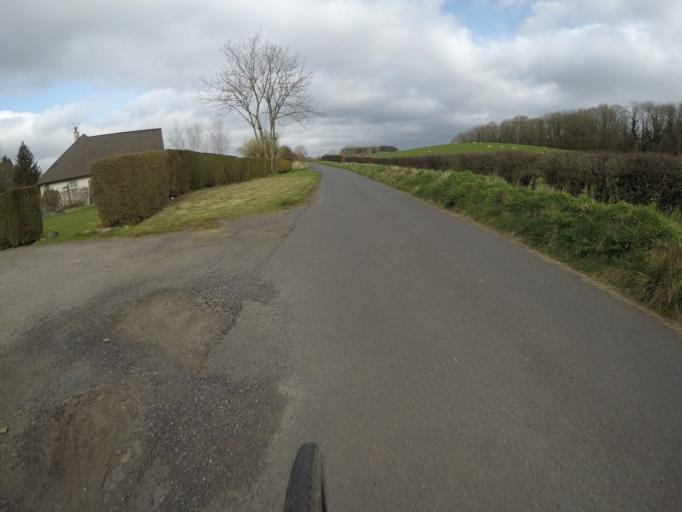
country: GB
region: Scotland
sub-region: North Ayrshire
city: Irvine
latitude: 55.6358
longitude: -4.6327
